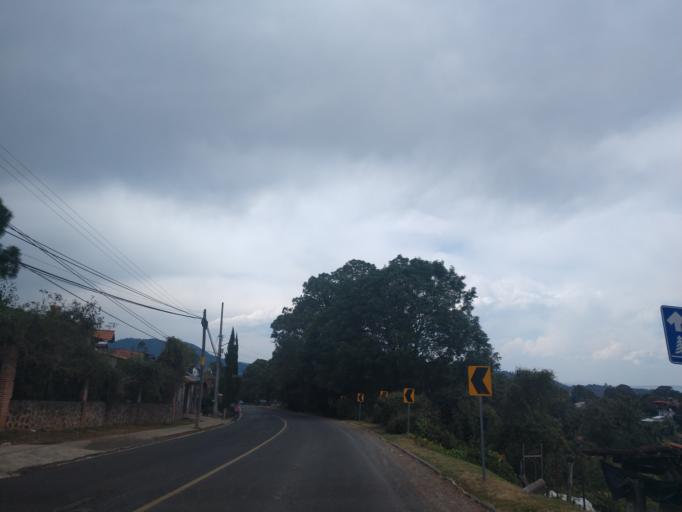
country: MX
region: Jalisco
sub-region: Mazamitla
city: Mazamitla
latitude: 19.9208
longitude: -103.0255
